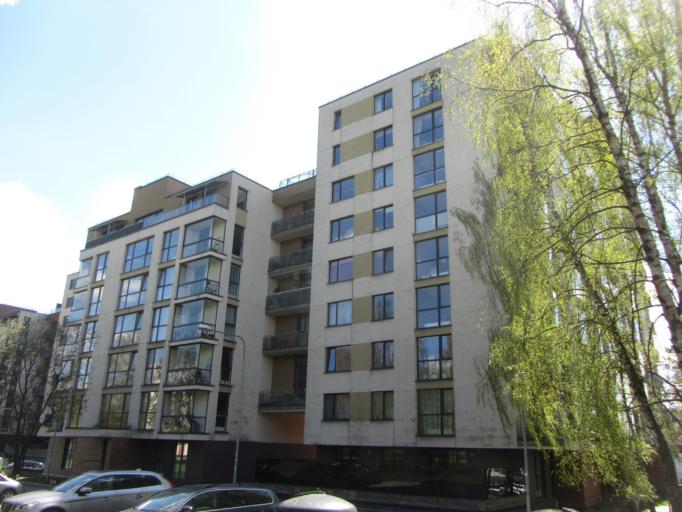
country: LT
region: Vilnius County
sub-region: Vilnius
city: Fabijoniskes
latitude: 54.7570
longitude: 25.2611
